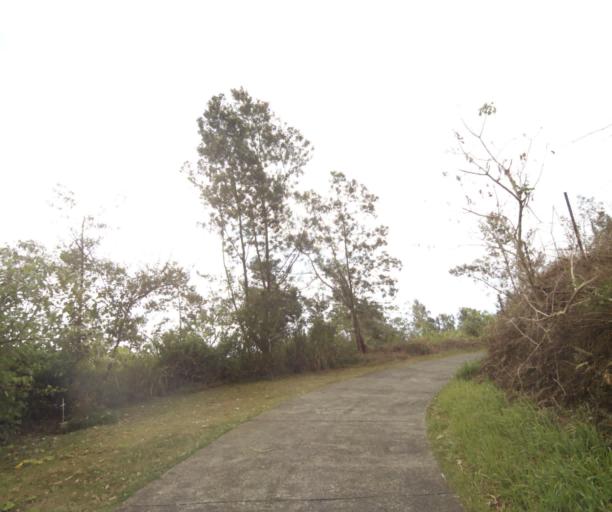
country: RE
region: Reunion
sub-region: Reunion
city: Saint-Paul
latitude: -21.0152
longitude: 55.3483
